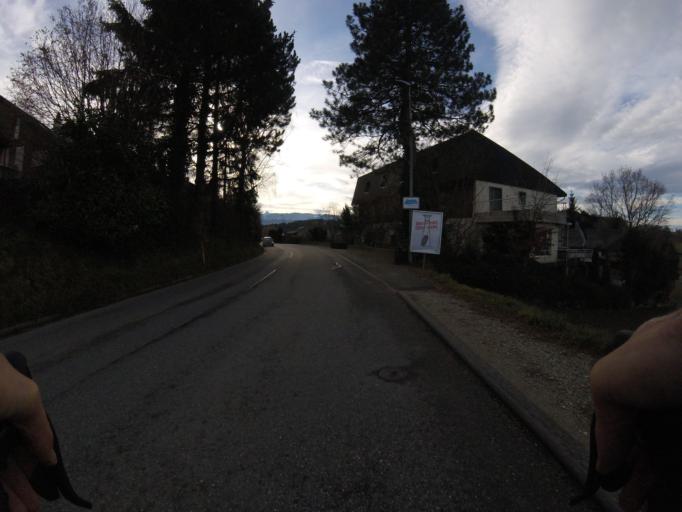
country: CH
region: Fribourg
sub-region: Sense District
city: Ueberstorf
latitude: 46.8541
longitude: 7.3157
